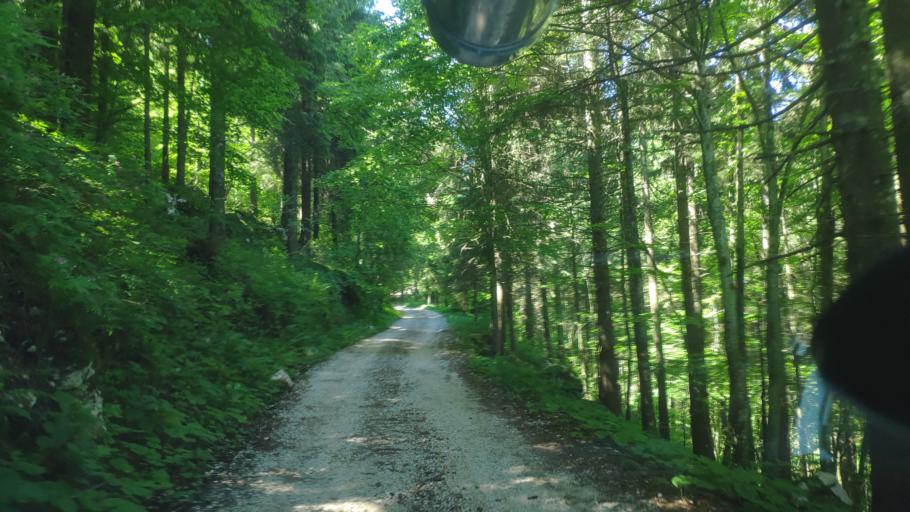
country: IT
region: Veneto
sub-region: Provincia di Vicenza
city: Caltrano
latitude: 45.8109
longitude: 11.4542
